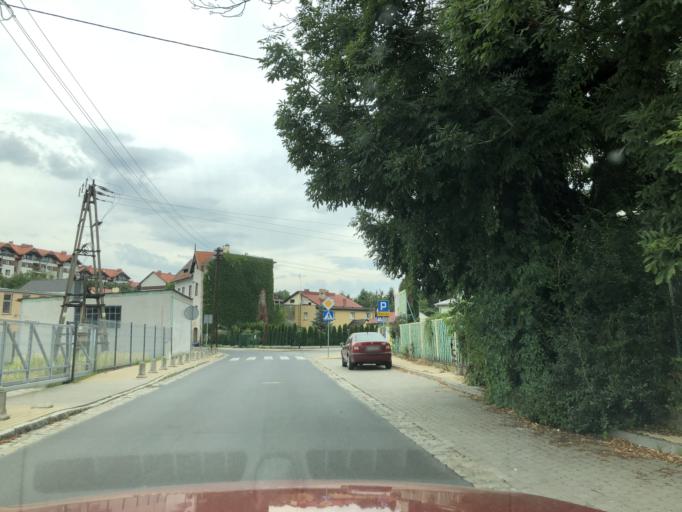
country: PL
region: Lower Silesian Voivodeship
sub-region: Powiat trzebnicki
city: Trzebnica
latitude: 51.3040
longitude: 17.0571
